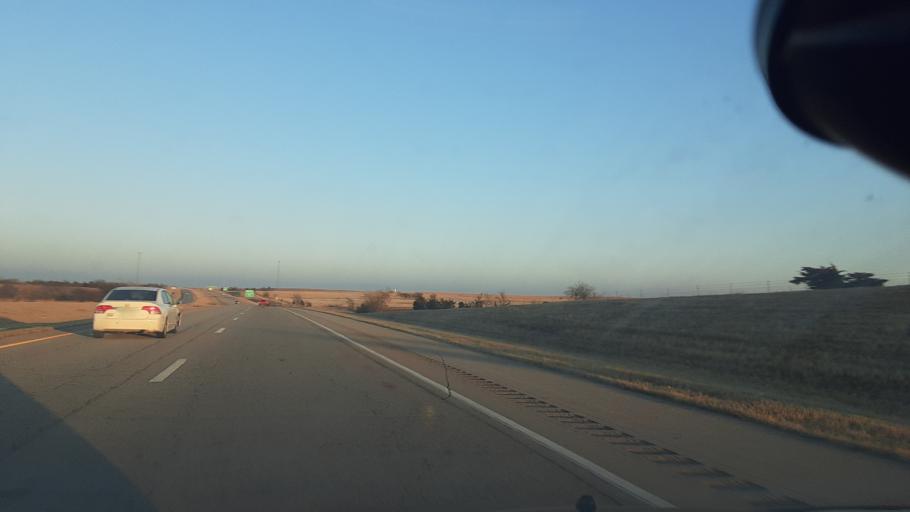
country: US
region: Oklahoma
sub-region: Noble County
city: Perry
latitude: 36.3980
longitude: -97.3572
